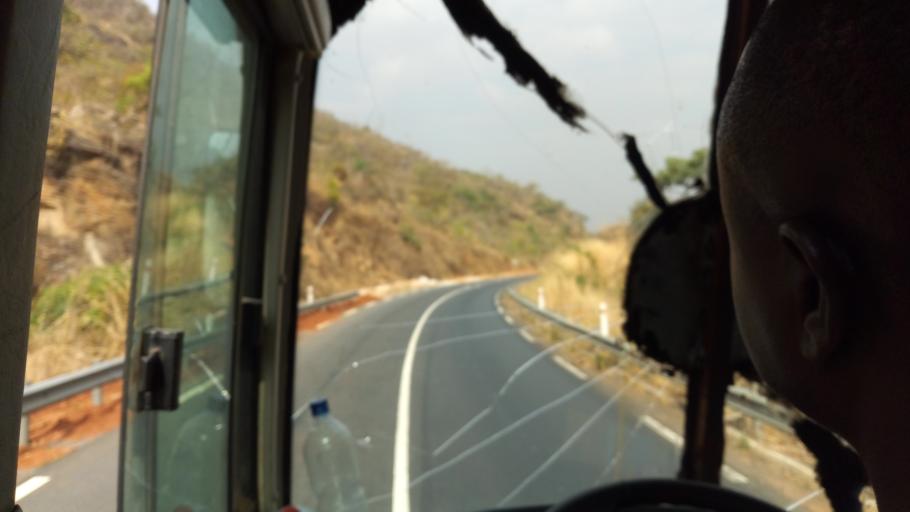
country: TG
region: Kara
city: Bafilo
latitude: 9.2507
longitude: 1.2166
